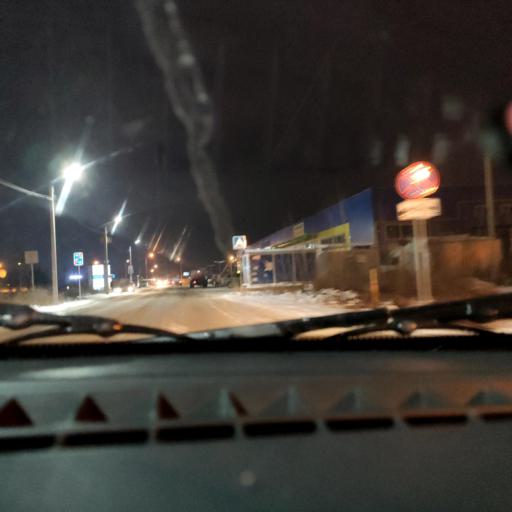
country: RU
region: Bashkortostan
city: Ufa
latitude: 54.6626
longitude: 56.0712
